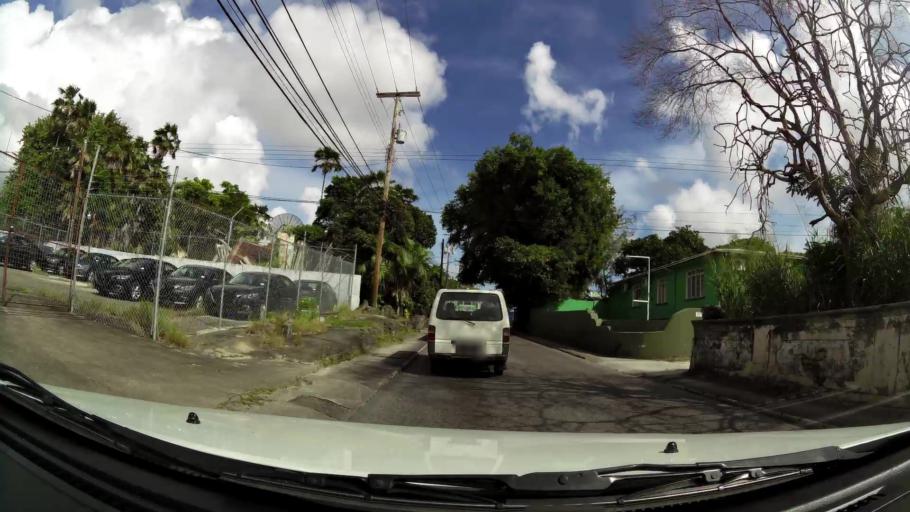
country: BB
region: Saint Michael
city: Bridgetown
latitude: 13.0939
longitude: -59.5978
